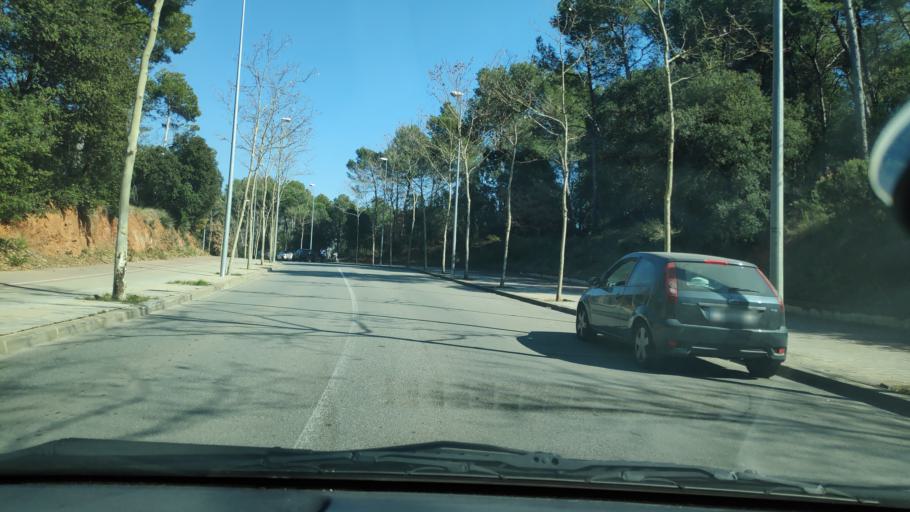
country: ES
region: Catalonia
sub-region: Provincia de Barcelona
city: Sant Quirze del Valles
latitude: 41.5547
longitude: 2.0700
